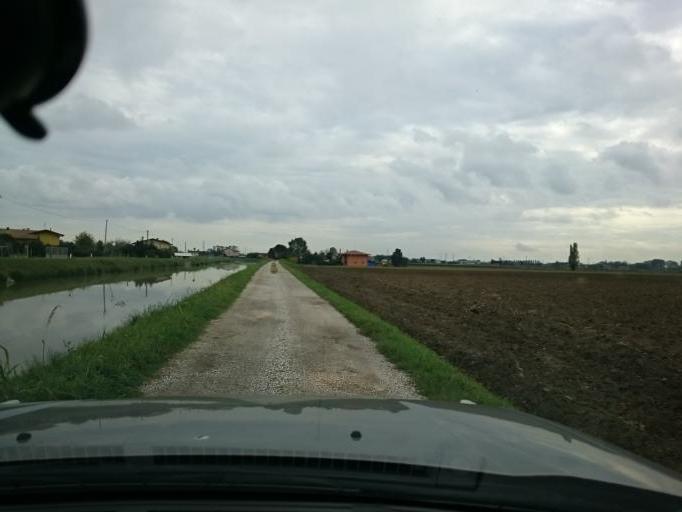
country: IT
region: Veneto
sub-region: Provincia di Padova
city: Codevigo
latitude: 45.2458
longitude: 12.1097
